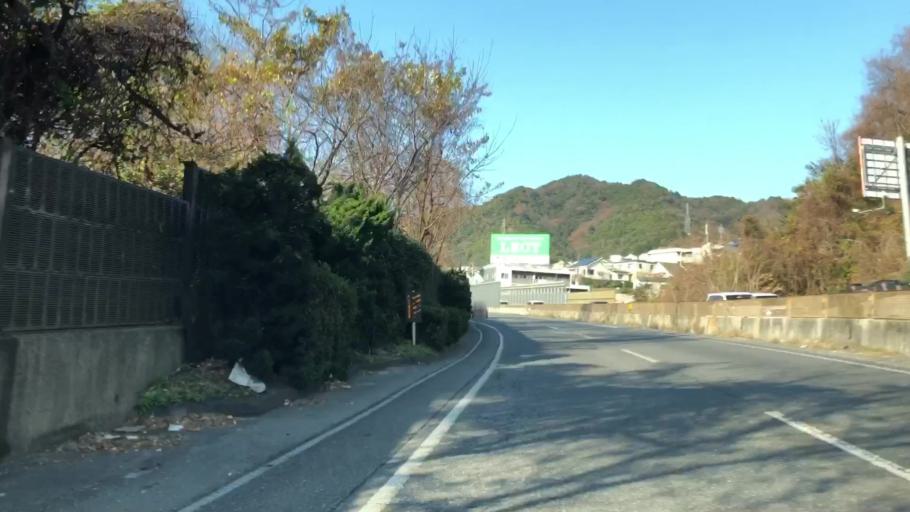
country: JP
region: Hiroshima
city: Hiroshima-shi
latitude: 34.3943
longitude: 132.4191
